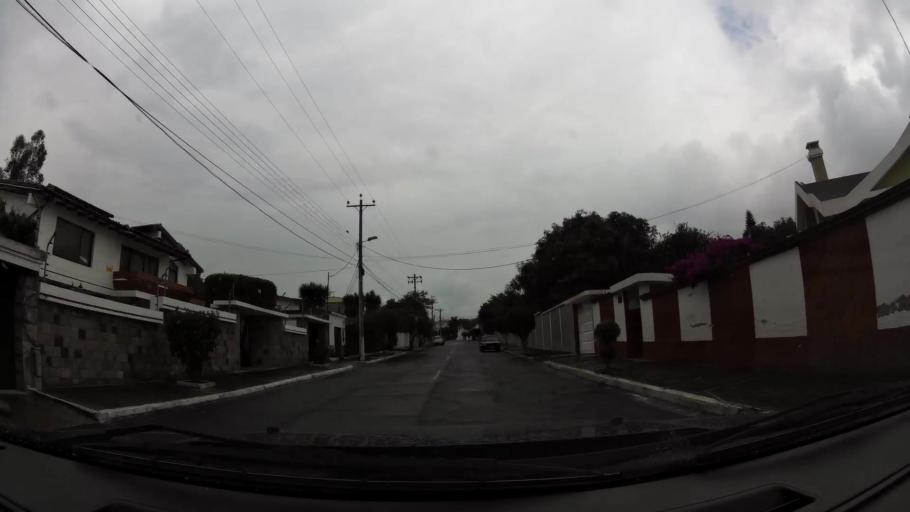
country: EC
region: Pichincha
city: Sangolqui
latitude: -0.3132
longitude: -78.4395
